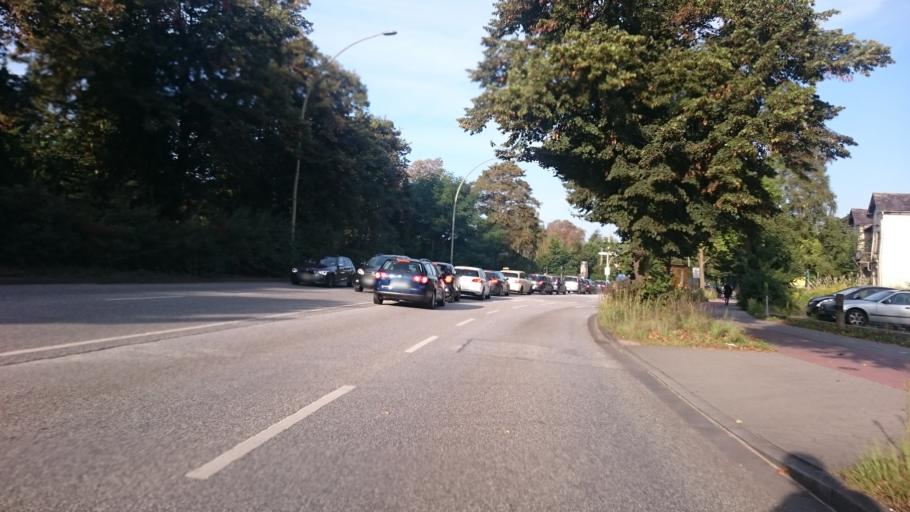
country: DE
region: Hamburg
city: Stellingen
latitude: 53.5708
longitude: 9.9198
